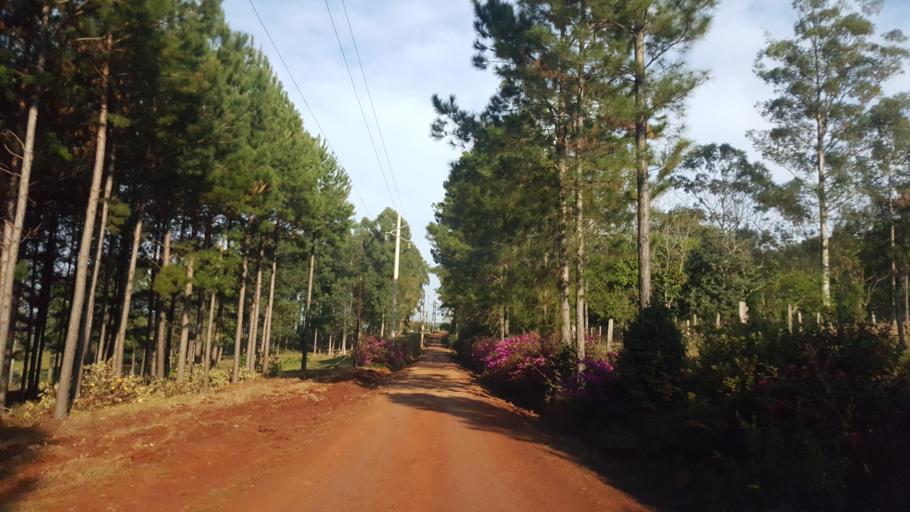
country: AR
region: Misiones
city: Capiovi
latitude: -26.9147
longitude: -55.0692
